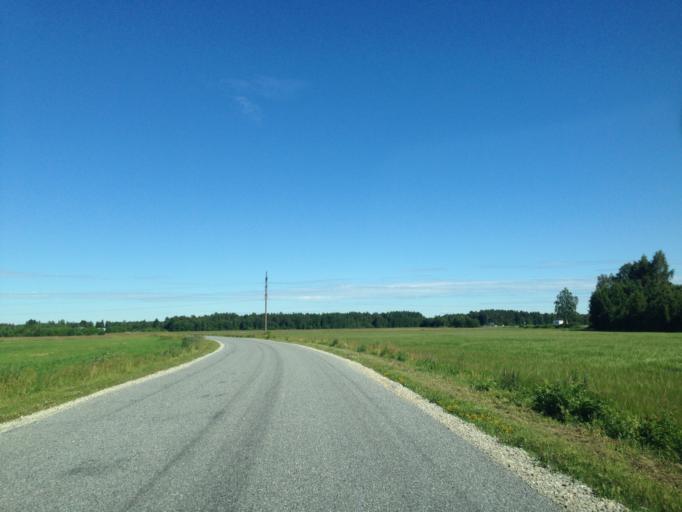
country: EE
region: Harju
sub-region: Raasiku vald
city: Raasiku
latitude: 59.4394
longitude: 25.1486
